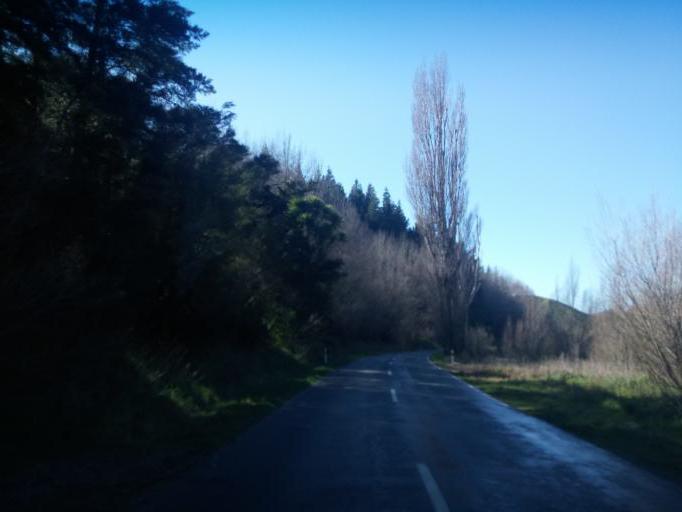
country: NZ
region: Wellington
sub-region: South Wairarapa District
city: Waipawa
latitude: -41.3830
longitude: 175.5011
